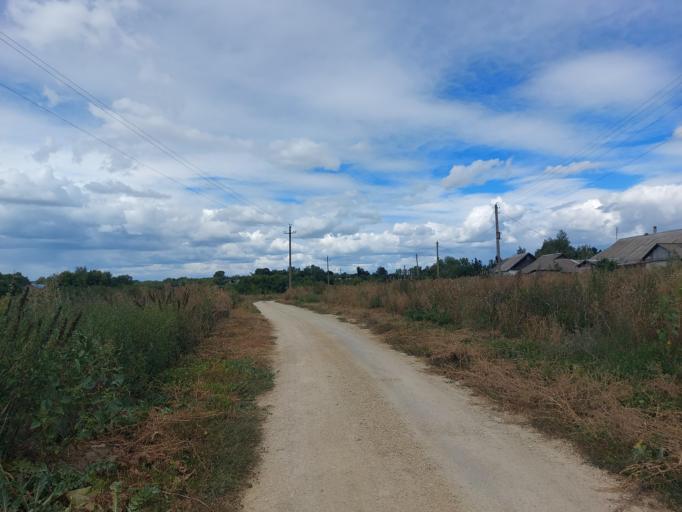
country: RU
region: Lipetsk
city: Terbuny
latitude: 52.2724
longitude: 38.2005
